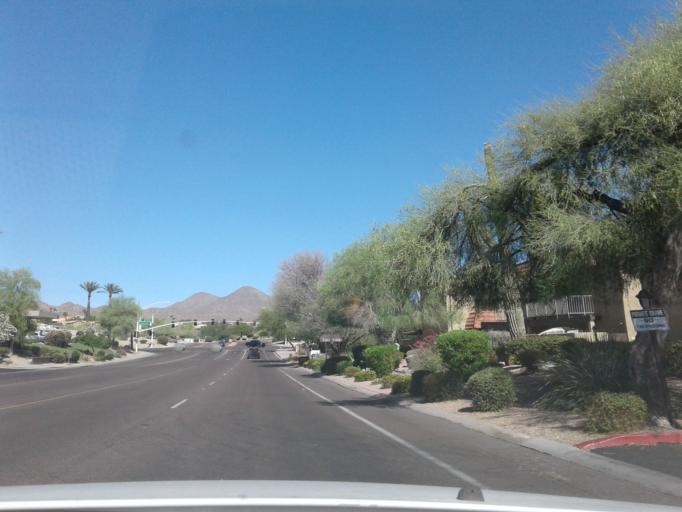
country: US
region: Arizona
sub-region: Maricopa County
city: Fountain Hills
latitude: 33.6110
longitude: -111.7273
